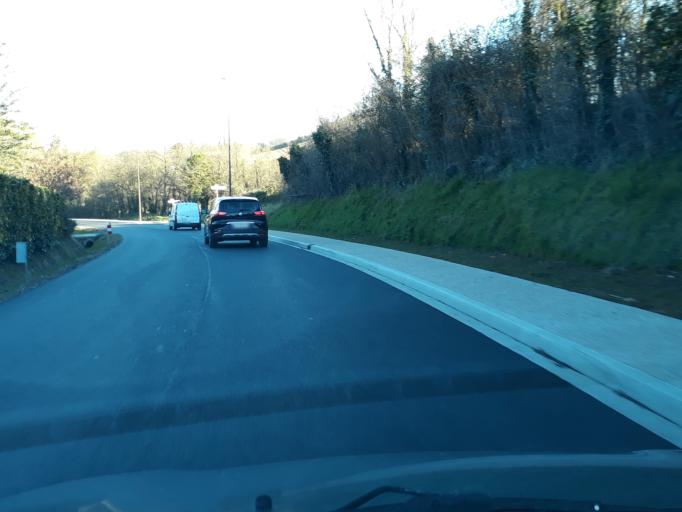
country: FR
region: Midi-Pyrenees
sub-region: Departement du Gers
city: Pavie
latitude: 43.6203
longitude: 0.6440
